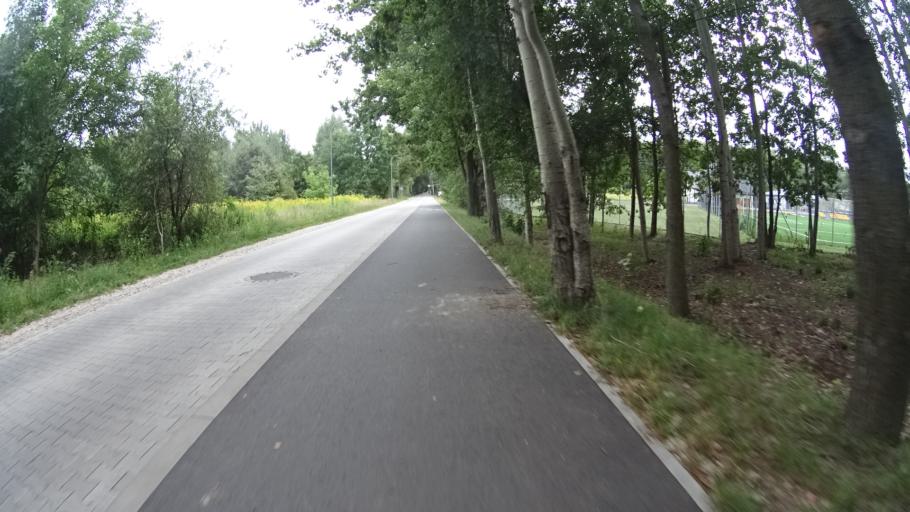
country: PL
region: Masovian Voivodeship
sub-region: Powiat pruszkowski
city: Granica
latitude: 52.1334
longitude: 20.8007
